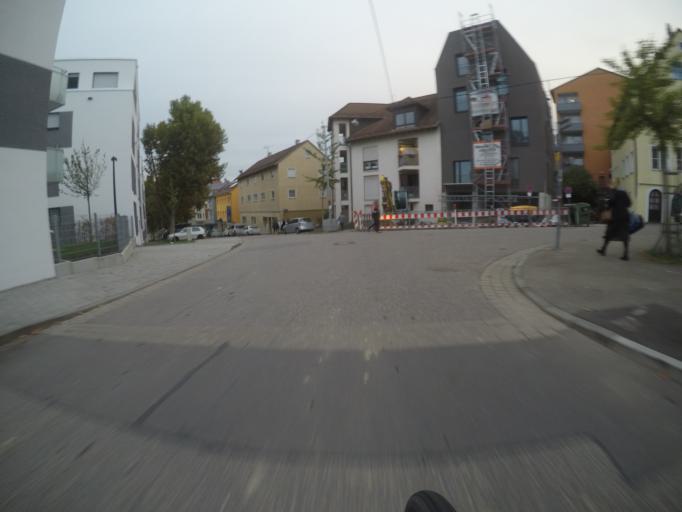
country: DE
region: Baden-Wuerttemberg
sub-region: Regierungsbezirk Stuttgart
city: Stuttgart-Ost
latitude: 48.7962
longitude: 9.2083
